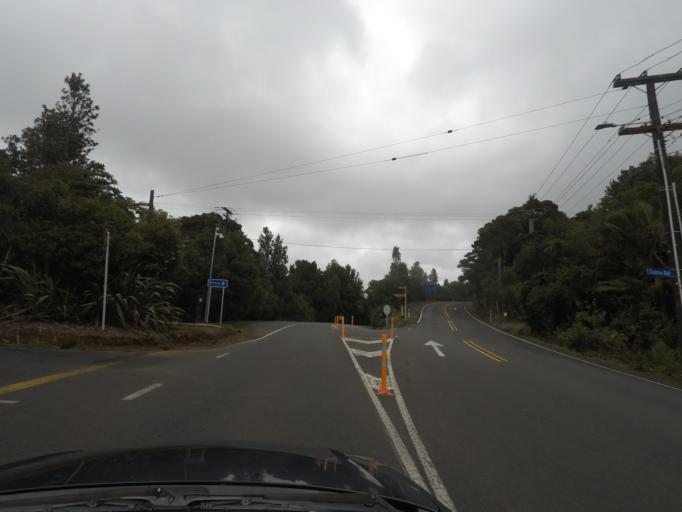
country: NZ
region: Auckland
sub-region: Auckland
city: Titirangi
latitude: -36.9329
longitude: 174.5751
